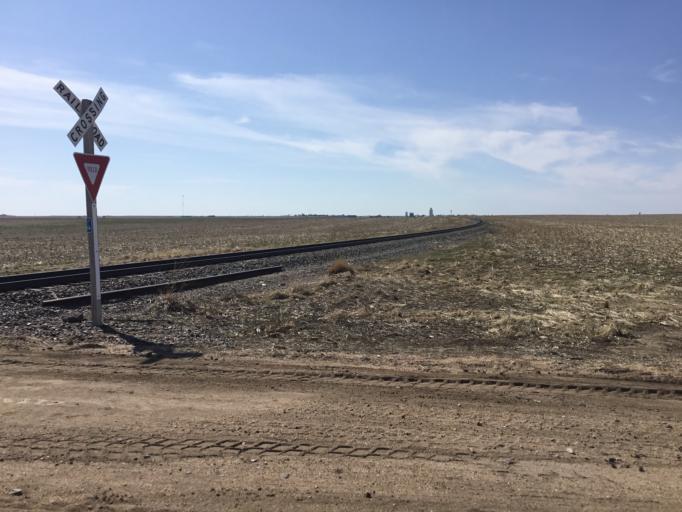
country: US
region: Kansas
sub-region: Trego County
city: WaKeeney
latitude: 39.0385
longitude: -100.0742
